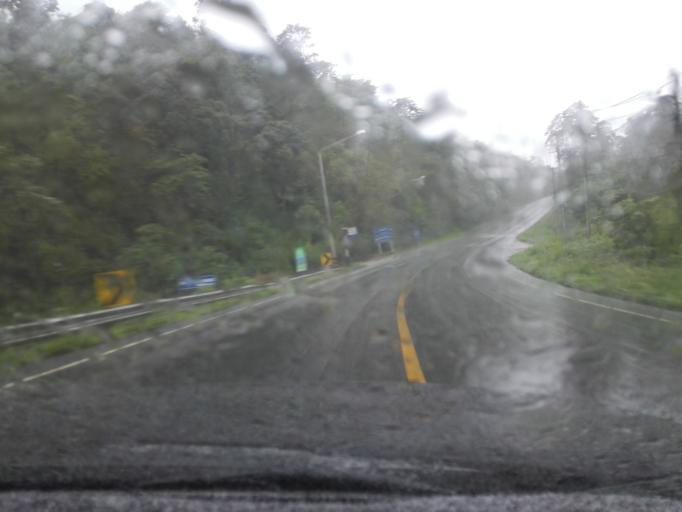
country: TH
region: Tak
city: Tak
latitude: 16.7575
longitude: 98.9216
